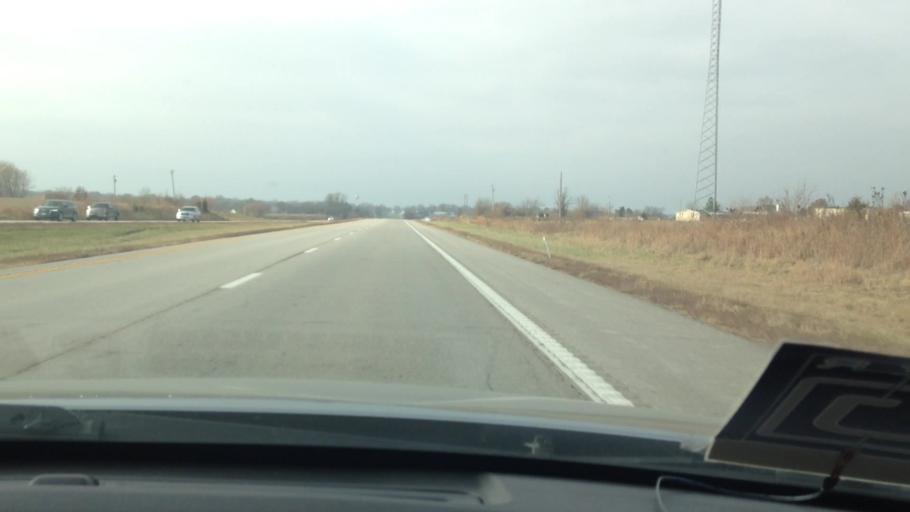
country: US
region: Missouri
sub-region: Cass County
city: Garden City
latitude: 38.5497
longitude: -94.1731
